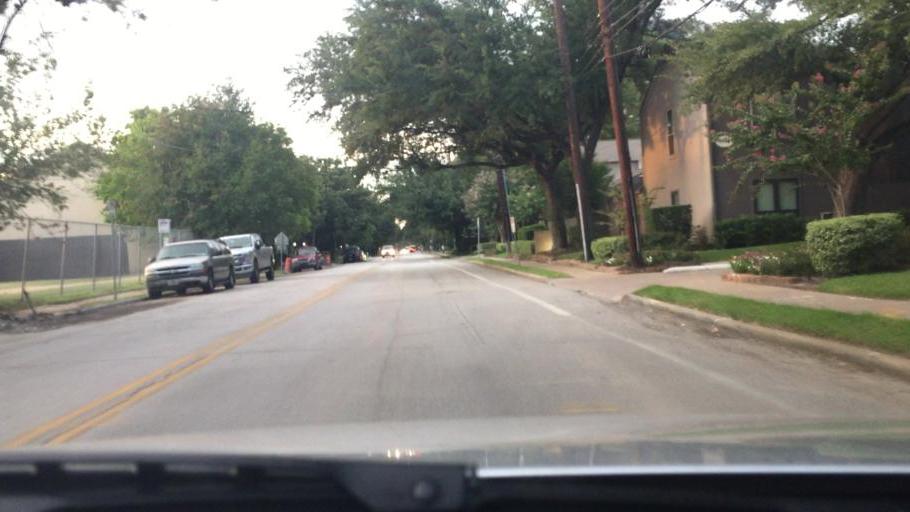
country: US
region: Texas
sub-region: Harris County
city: Hunters Creek Village
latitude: 29.7528
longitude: -95.4796
